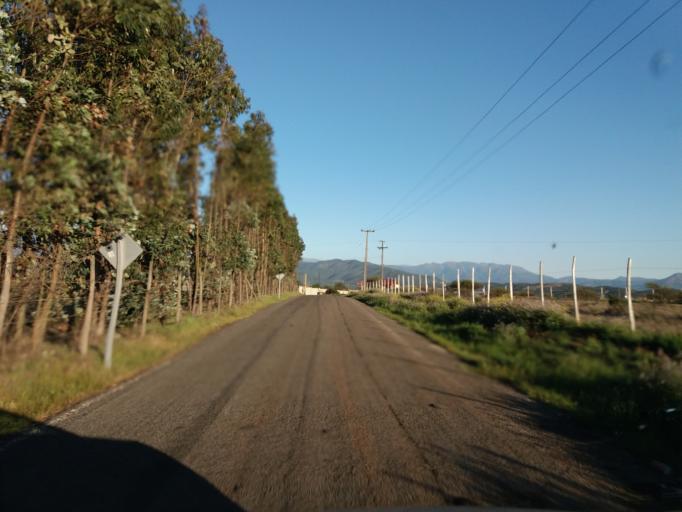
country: CL
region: Valparaiso
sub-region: Provincia de Quillota
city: Quillota
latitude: -32.9164
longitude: -71.3332
